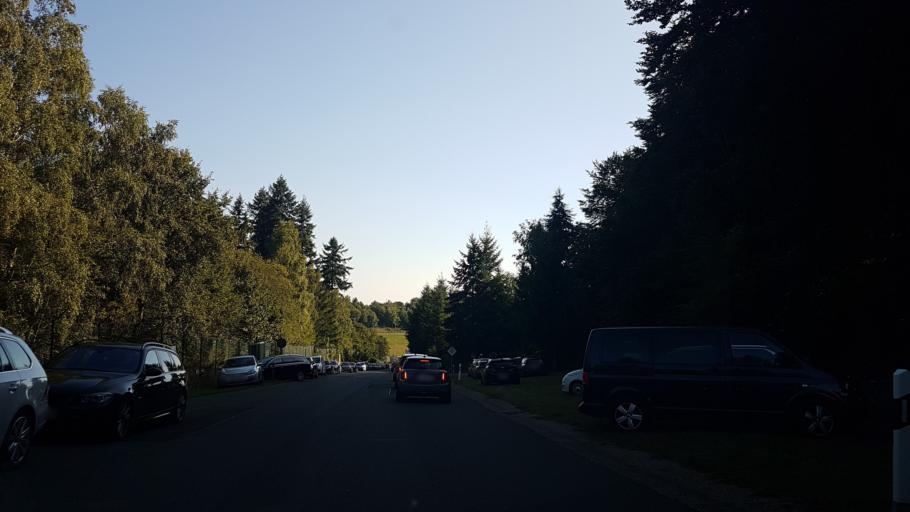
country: DE
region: Rheinland-Pfalz
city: Baumholder
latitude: 49.6296
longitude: 7.3152
